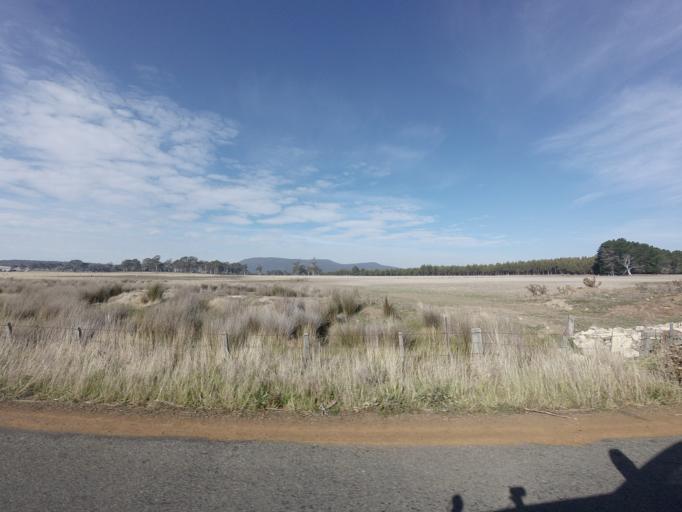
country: AU
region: Tasmania
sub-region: Sorell
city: Sorell
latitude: -42.4413
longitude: 147.4710
